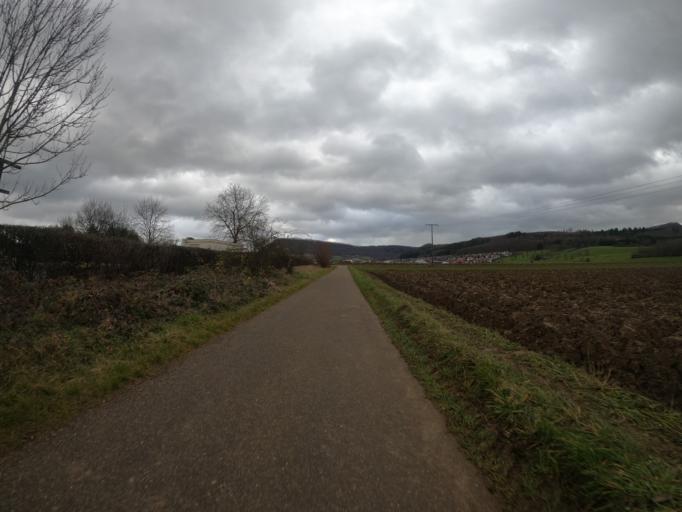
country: DE
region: Baden-Wuerttemberg
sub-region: Regierungsbezirk Stuttgart
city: Gingen an der Fils
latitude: 48.6832
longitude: 9.7820
